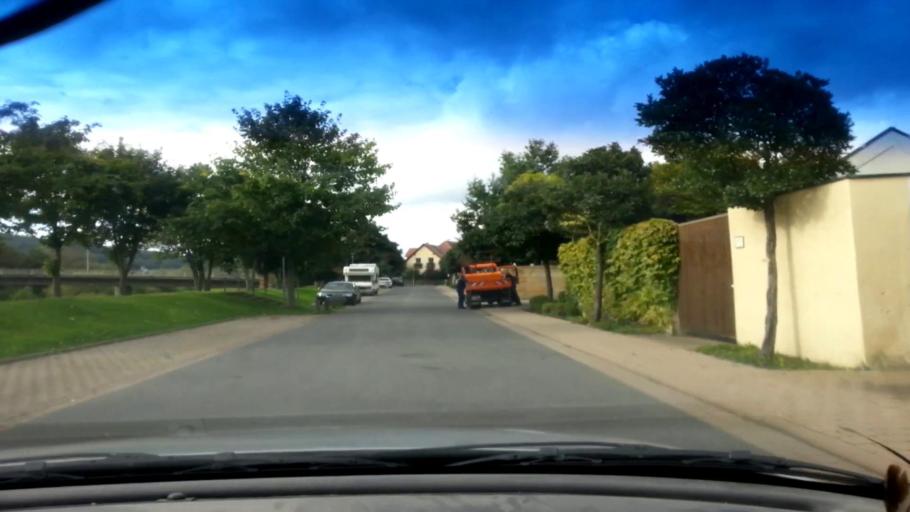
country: DE
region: Bavaria
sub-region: Upper Franconia
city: Kemmern
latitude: 49.9508
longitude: 10.8752
